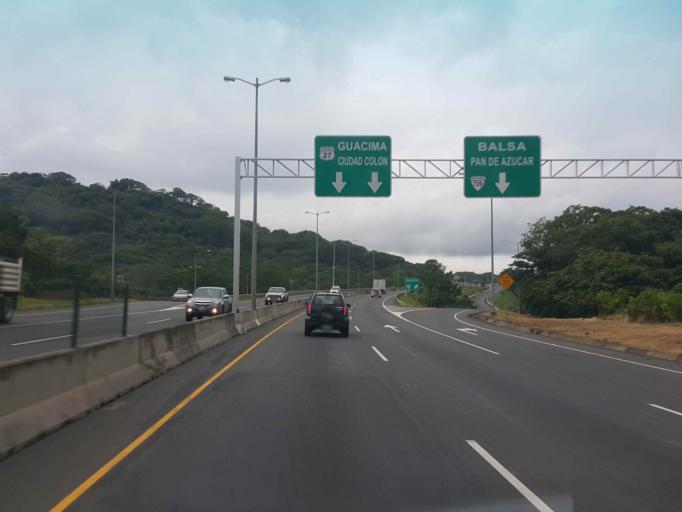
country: CR
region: Alajuela
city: Atenas
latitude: 9.9433
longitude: -84.3794
